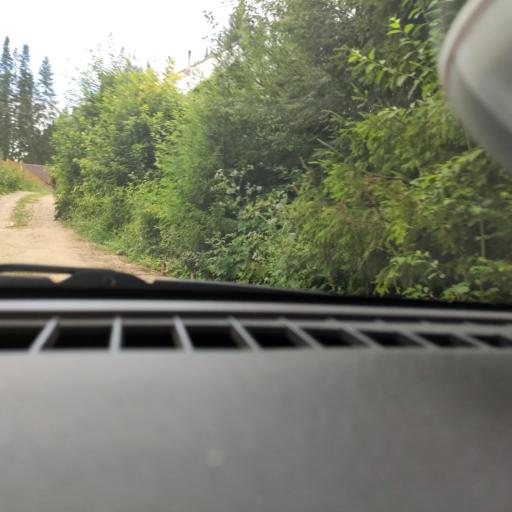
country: RU
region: Perm
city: Polazna
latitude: 58.3493
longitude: 56.2458
